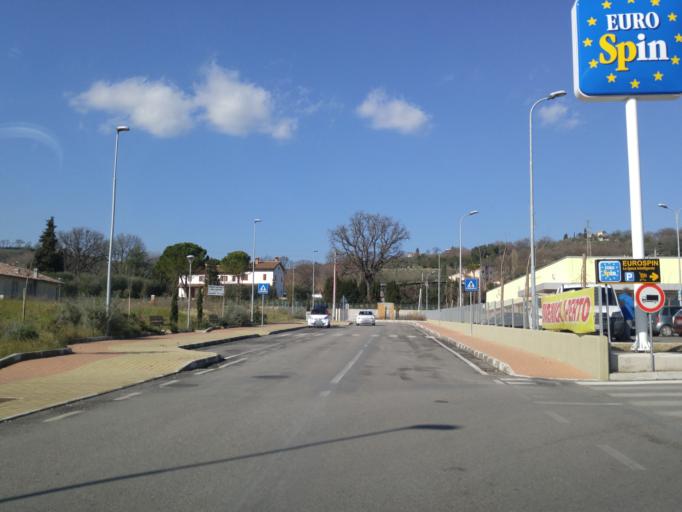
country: IT
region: The Marches
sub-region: Provincia di Pesaro e Urbino
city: Fossombrone
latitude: 43.7026
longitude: 12.8327
